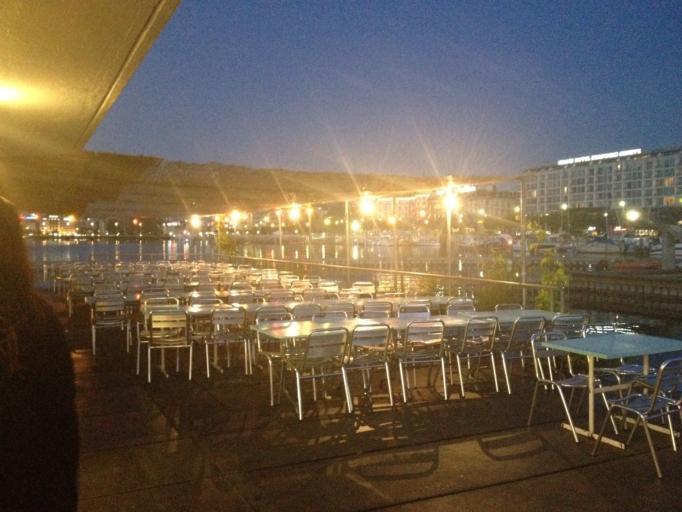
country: CH
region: Geneva
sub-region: Geneva
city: Geneve
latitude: 46.2105
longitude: 6.1533
